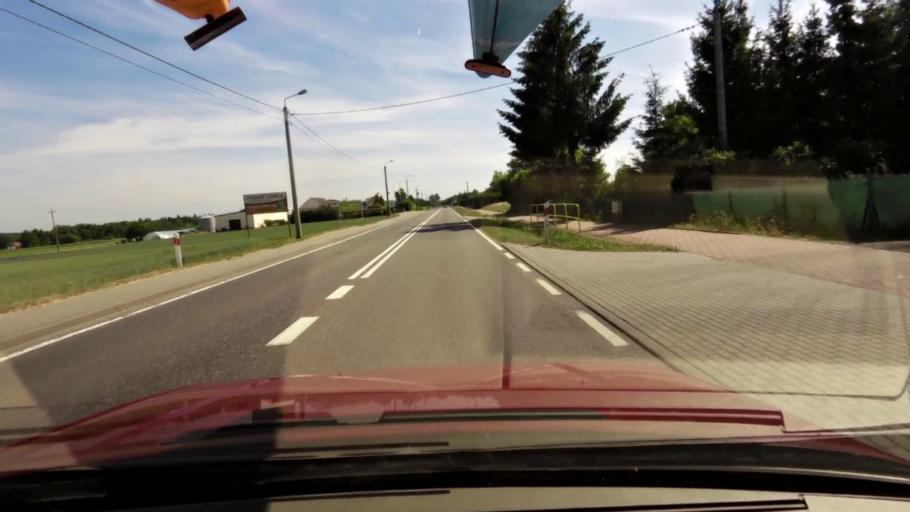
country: PL
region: Pomeranian Voivodeship
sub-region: Powiat slupski
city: Kobylnica
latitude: 54.4194
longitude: 17.0074
